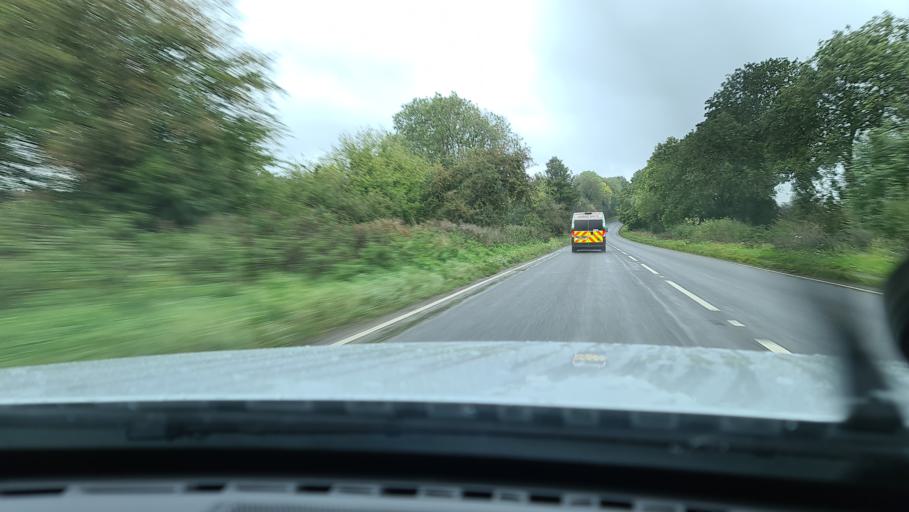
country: GB
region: England
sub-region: Oxfordshire
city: Deddington
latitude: 51.9984
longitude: -1.3217
